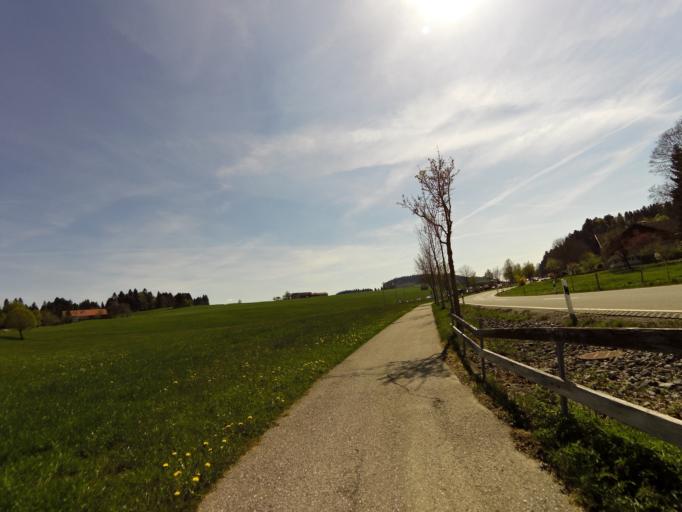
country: DE
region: Bavaria
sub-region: Swabia
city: Oberreute
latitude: 47.5954
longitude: 9.9530
